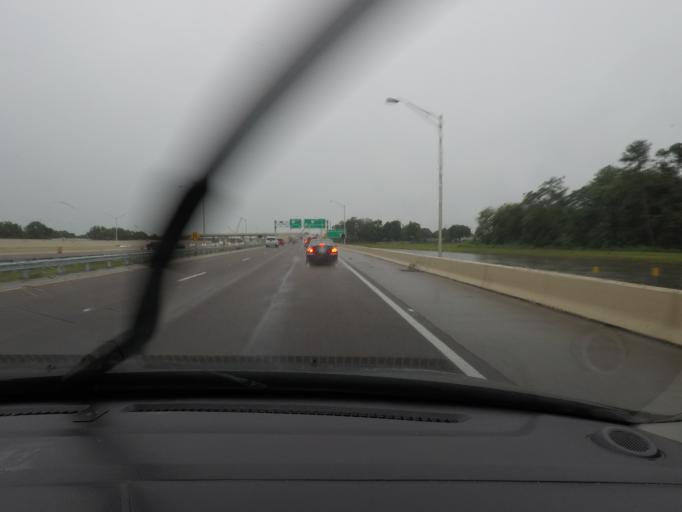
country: US
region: Florida
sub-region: Orange County
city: Union Park
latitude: 28.5471
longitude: -81.2677
